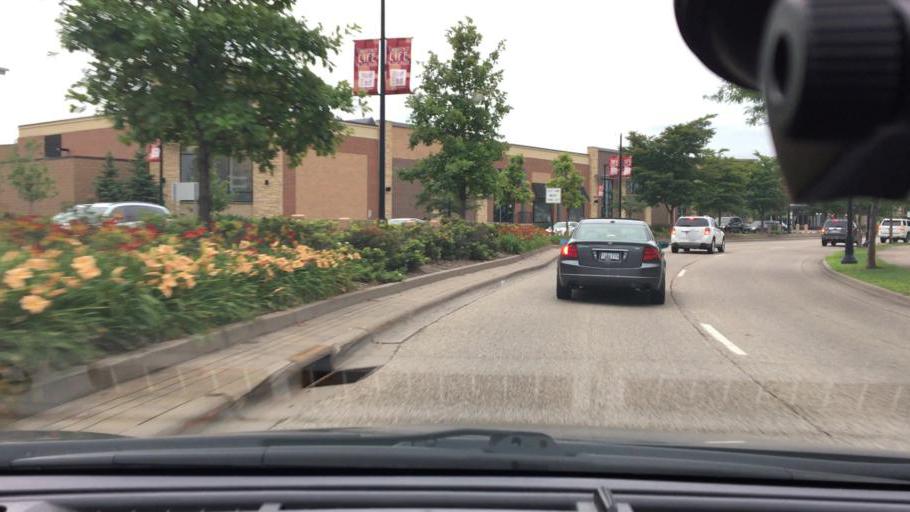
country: US
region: Minnesota
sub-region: Hennepin County
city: Saint Louis Park
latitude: 44.9689
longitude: -93.3500
